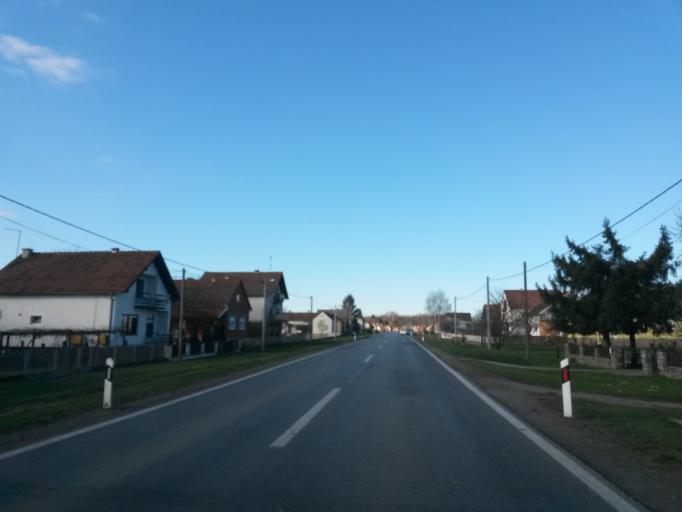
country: HR
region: Virovitick-Podravska
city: Suhopolje
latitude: 45.7929
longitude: 17.5108
